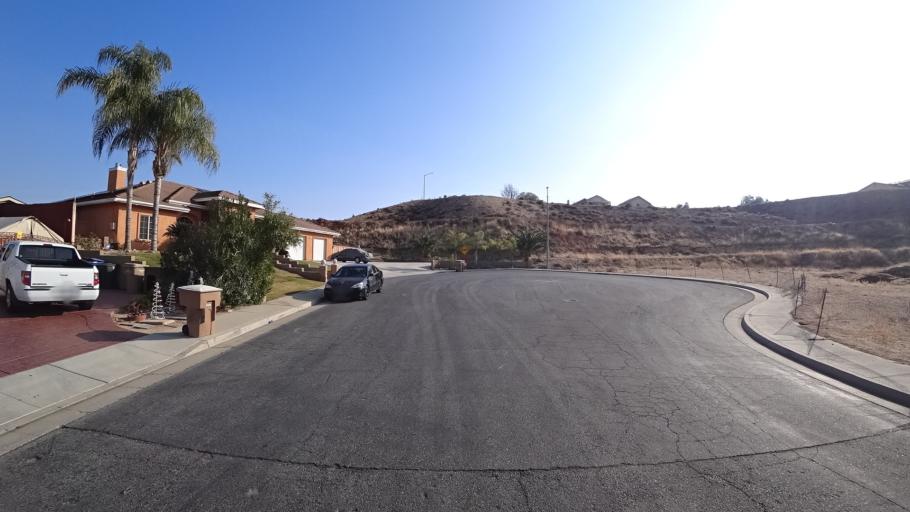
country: US
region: California
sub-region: Kern County
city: Oildale
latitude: 35.4069
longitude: -118.9355
